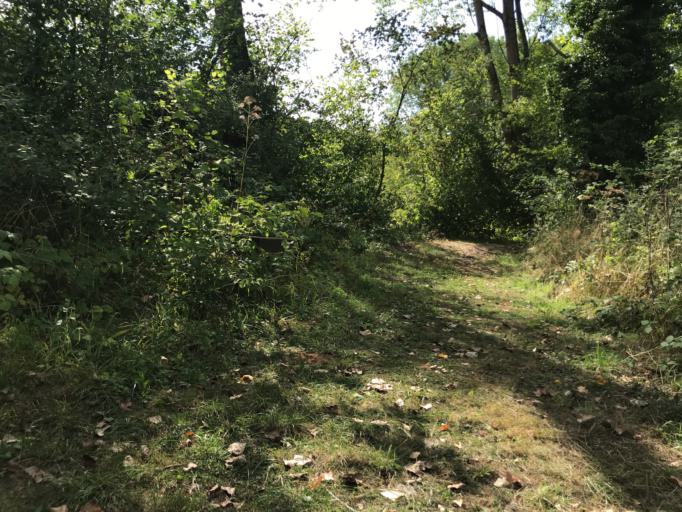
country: FR
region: Lorraine
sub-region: Departement de Meurthe-et-Moselle
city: Thil
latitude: 49.4947
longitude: 5.9129
